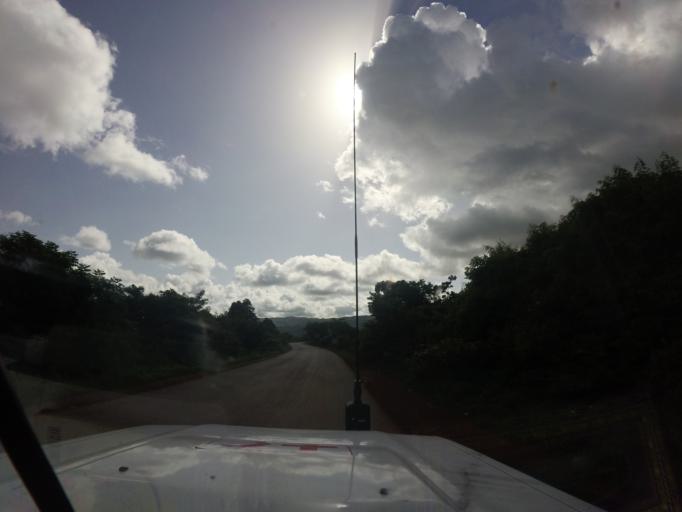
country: GN
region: Mamou
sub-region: Mamou Prefecture
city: Mamou
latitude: 10.3523
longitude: -12.2138
